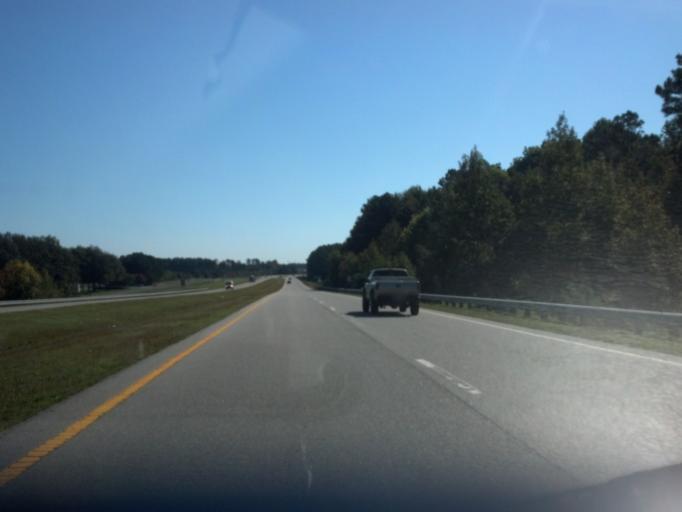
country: US
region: North Carolina
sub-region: Pitt County
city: Greenville
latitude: 35.6587
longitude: -77.3620
